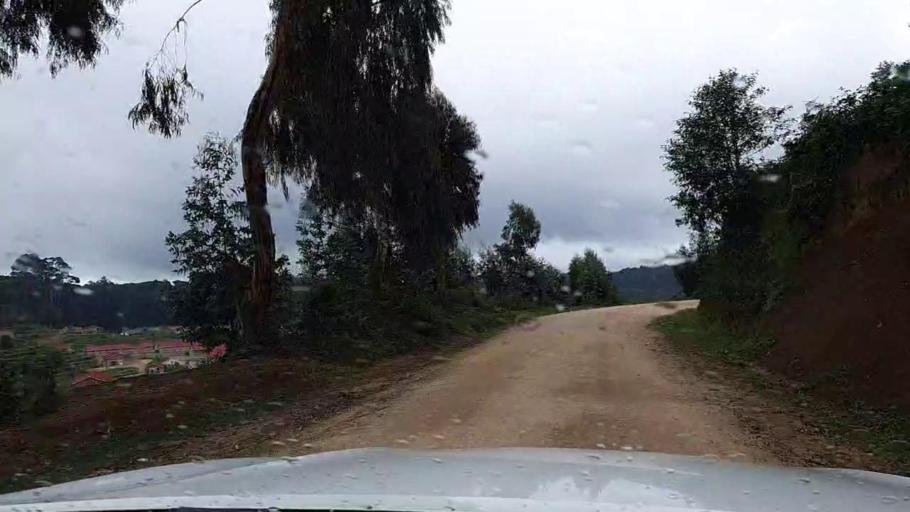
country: RW
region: Southern Province
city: Nzega
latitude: -2.3722
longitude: 29.3809
